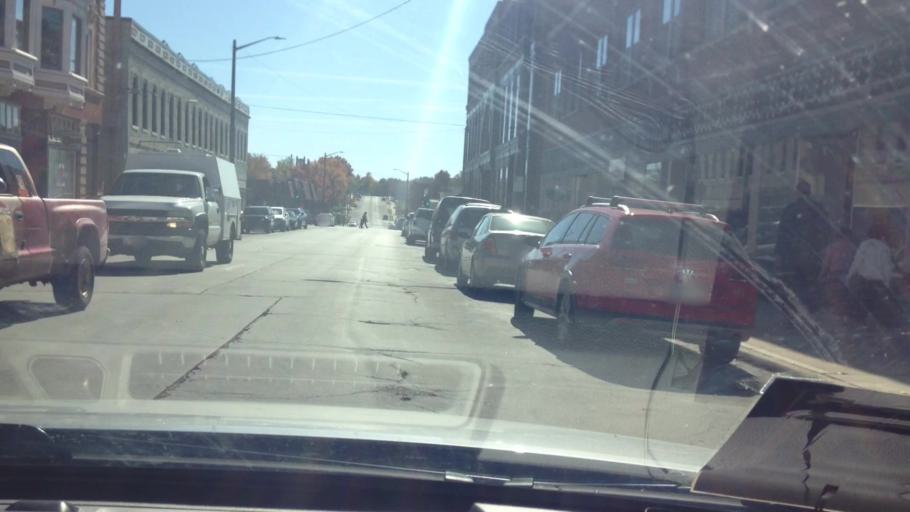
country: US
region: Kansas
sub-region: Leavenworth County
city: Leavenworth
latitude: 39.3179
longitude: -94.9153
